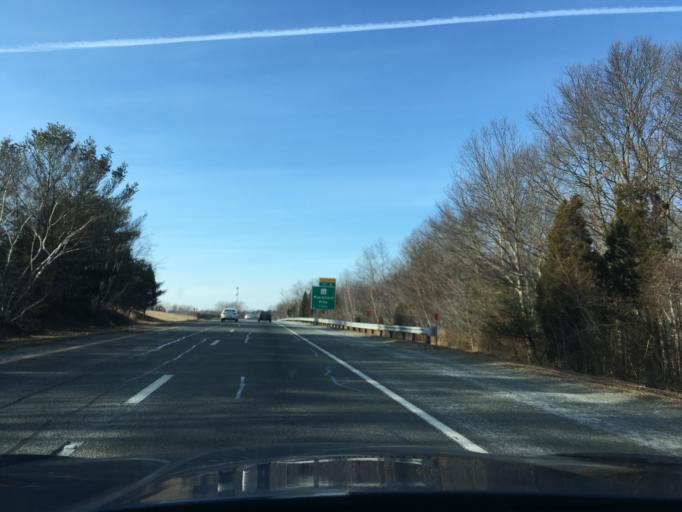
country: US
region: Rhode Island
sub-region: Providence County
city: Johnston
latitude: 41.7744
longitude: -71.4903
